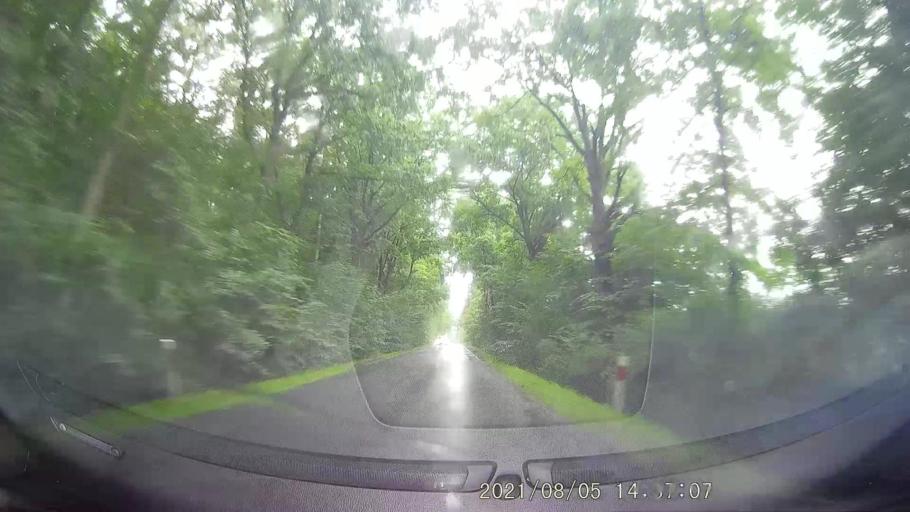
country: PL
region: Opole Voivodeship
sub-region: Powiat nyski
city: Lambinowice
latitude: 50.4660
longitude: 17.4788
